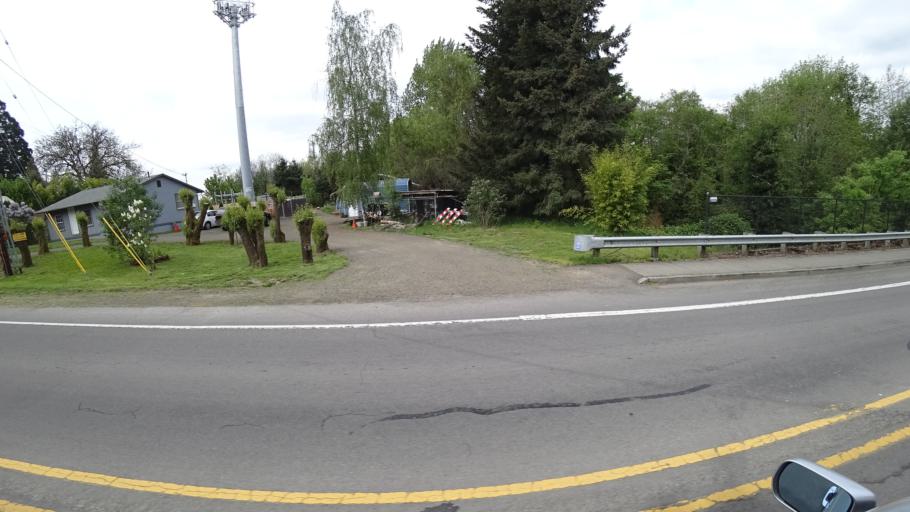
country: US
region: Oregon
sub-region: Washington County
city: Hillsboro
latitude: 45.5346
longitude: -122.9930
